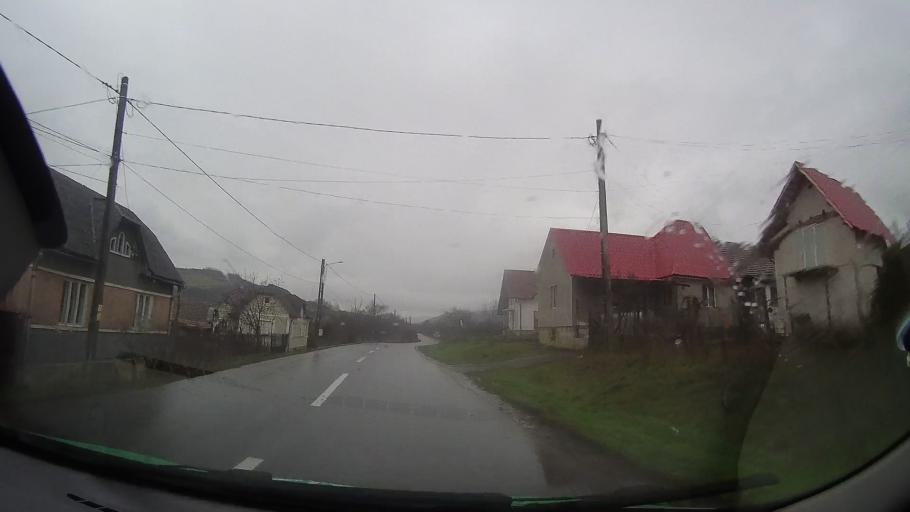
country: RO
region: Bistrita-Nasaud
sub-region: Comuna Mariselu
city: Mariselu
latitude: 47.0150
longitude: 24.5508
